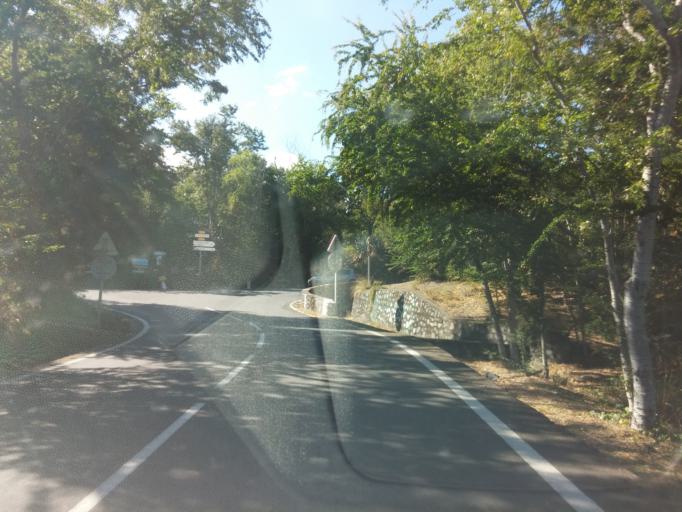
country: RE
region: Reunion
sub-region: Reunion
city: Les Avirons
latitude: -21.2595
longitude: 55.3409
